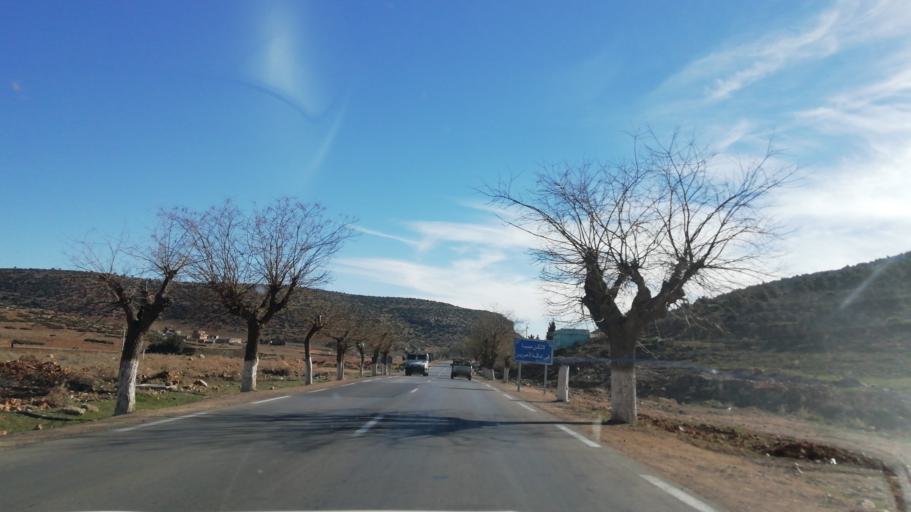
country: DZ
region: Tlemcen
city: Sebdou
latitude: 34.7031
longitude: -1.3166
